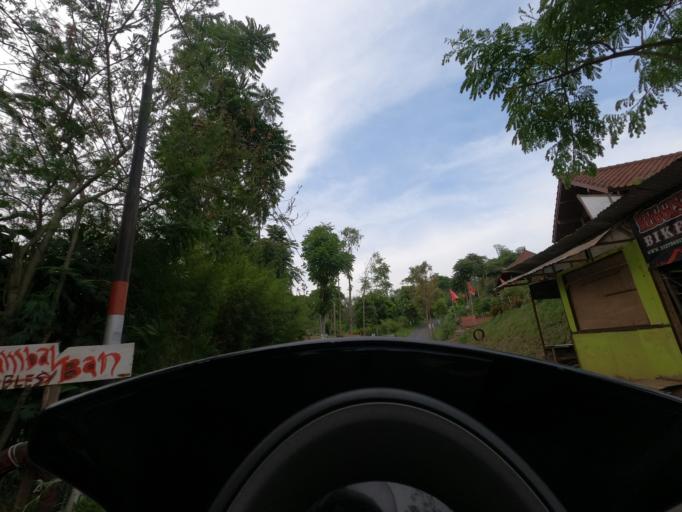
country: ID
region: West Java
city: Lembang
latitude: -6.8381
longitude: 107.6196
